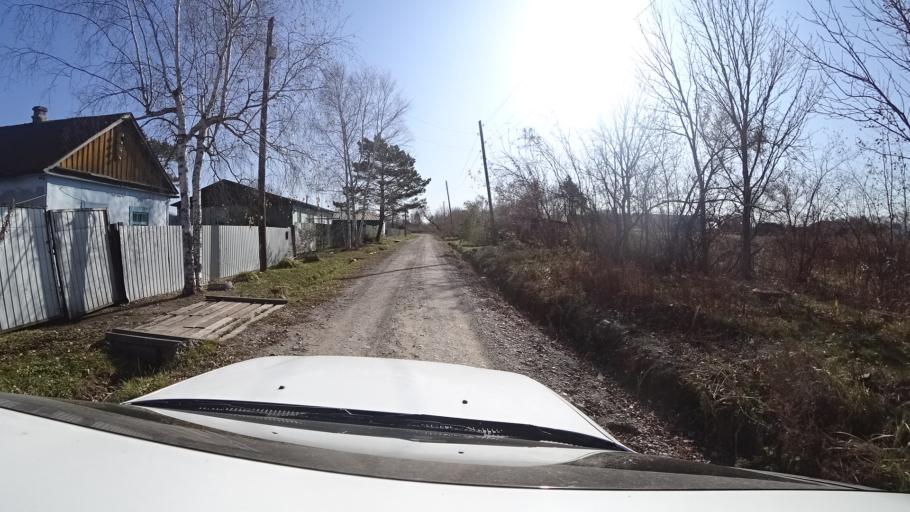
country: RU
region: Primorskiy
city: Lazo
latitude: 45.8804
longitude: 133.6437
